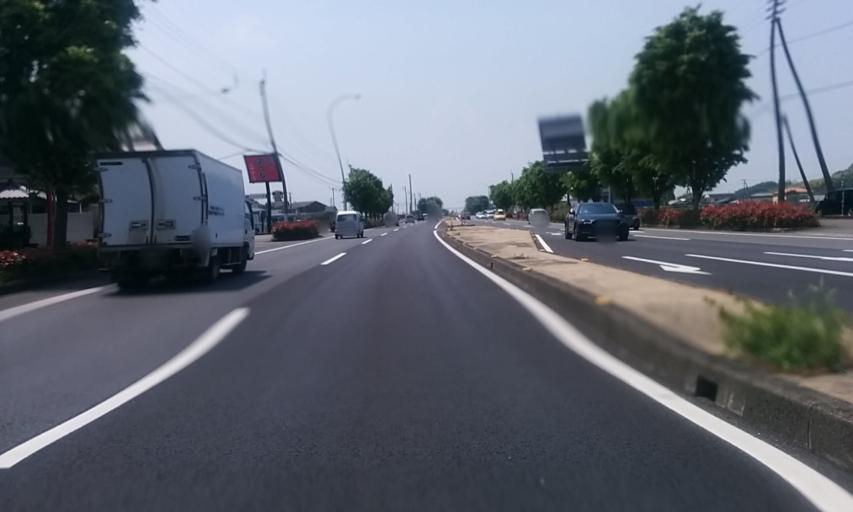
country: JP
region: Ehime
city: Saijo
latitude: 33.9213
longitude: 133.2496
